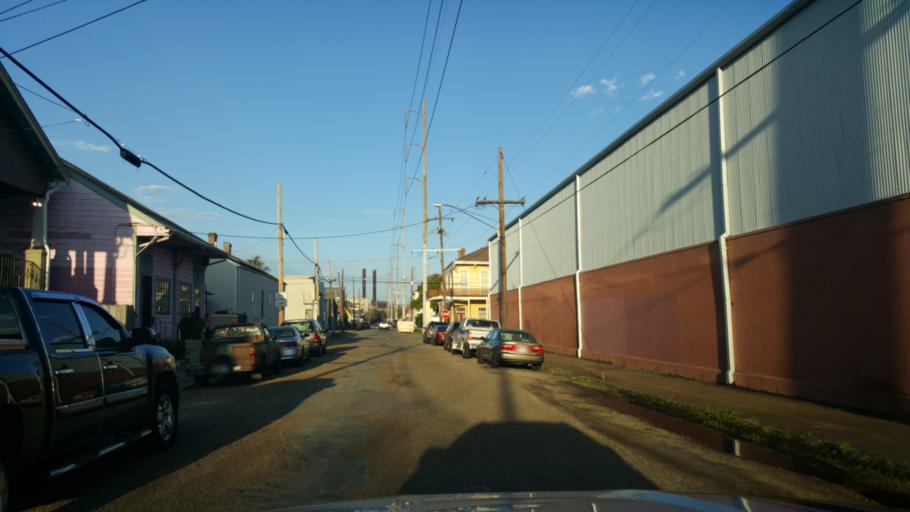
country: US
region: Louisiana
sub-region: Jefferson Parish
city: Harvey
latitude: 29.9237
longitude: -90.0741
